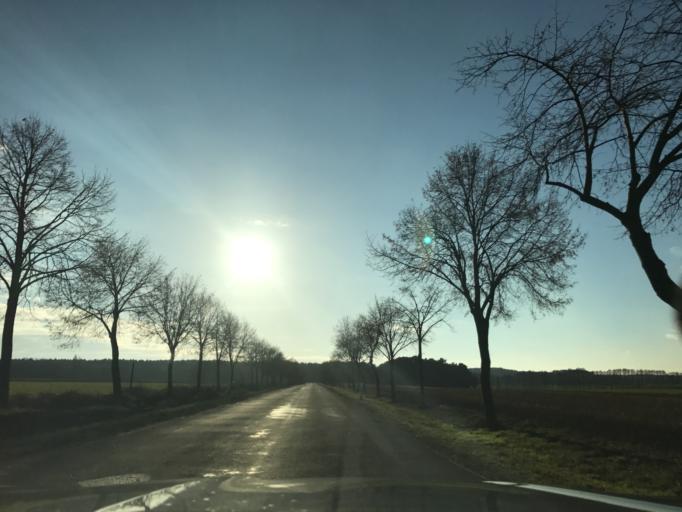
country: DE
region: Saxony-Anhalt
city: Loburg
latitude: 52.1773
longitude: 12.0430
